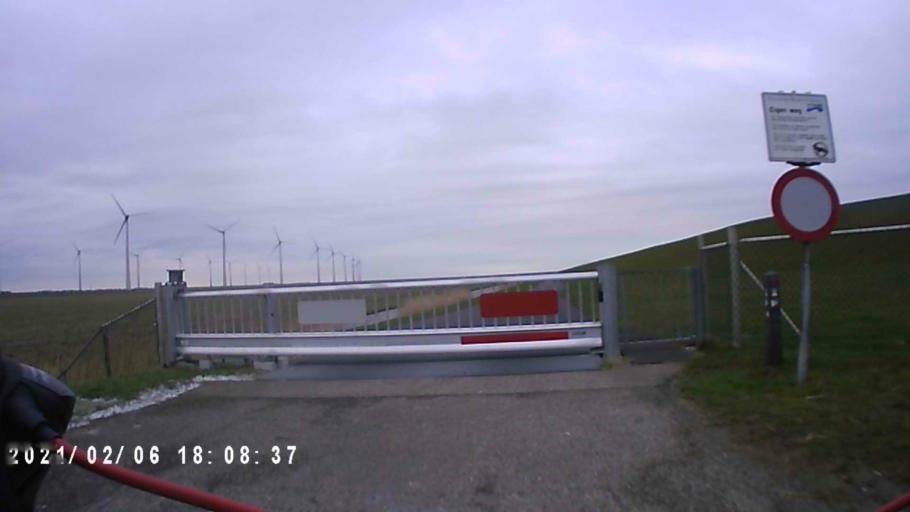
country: NL
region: Groningen
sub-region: Gemeente Appingedam
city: Appingedam
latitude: 53.4537
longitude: 6.7969
